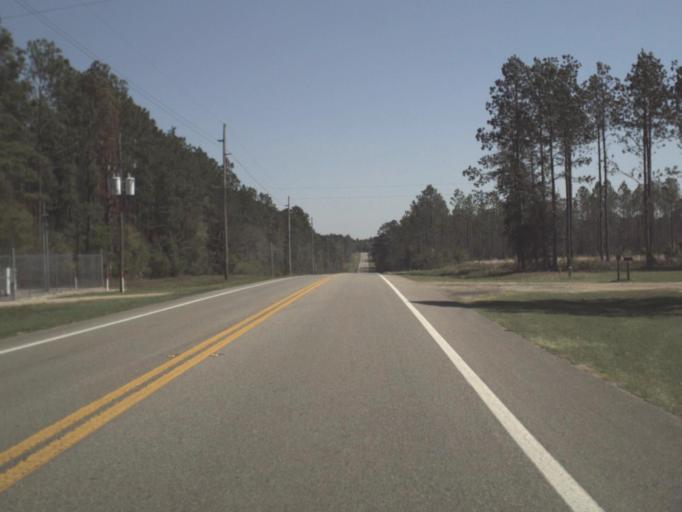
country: US
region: Florida
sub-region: Liberty County
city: Bristol
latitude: 30.4015
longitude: -84.8156
